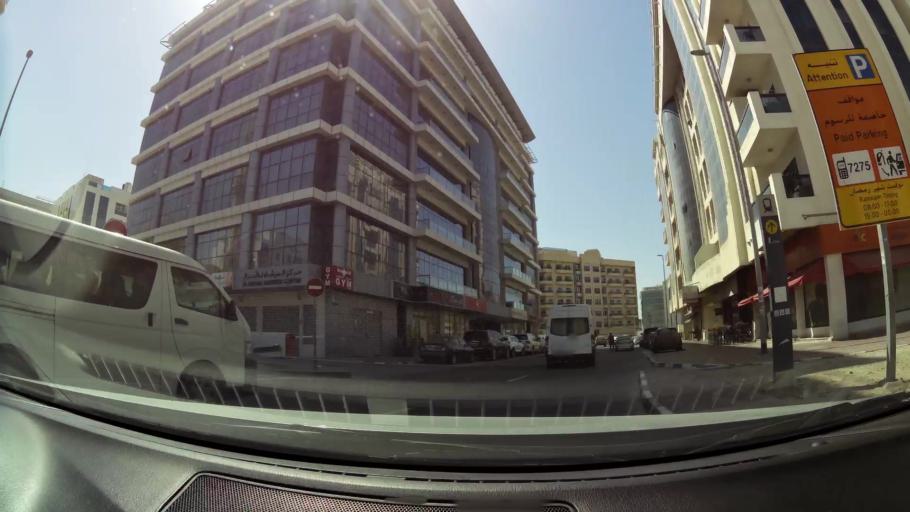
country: AE
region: Dubai
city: Dubai
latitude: 25.1133
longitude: 55.1944
